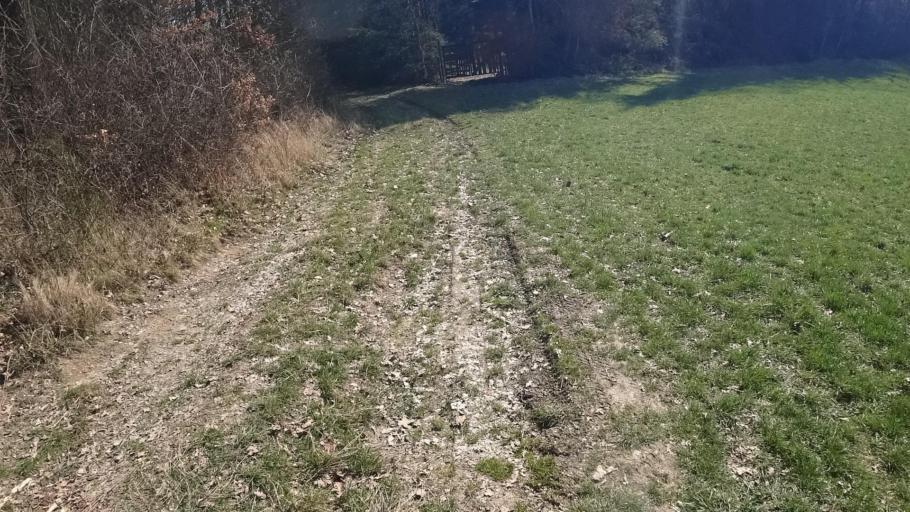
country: DE
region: Rheinland-Pfalz
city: Rheinbollen
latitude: 50.0189
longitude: 7.6765
